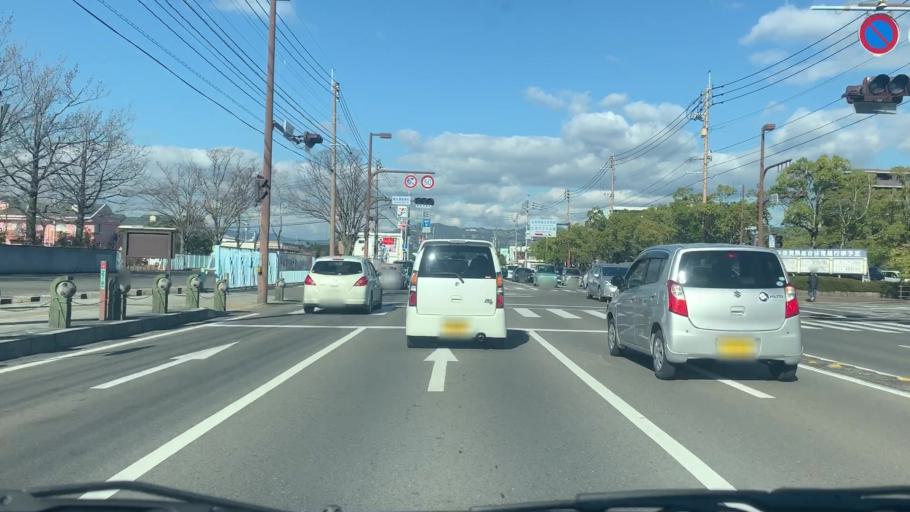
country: JP
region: Saga Prefecture
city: Saga-shi
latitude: 33.2772
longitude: 130.2930
